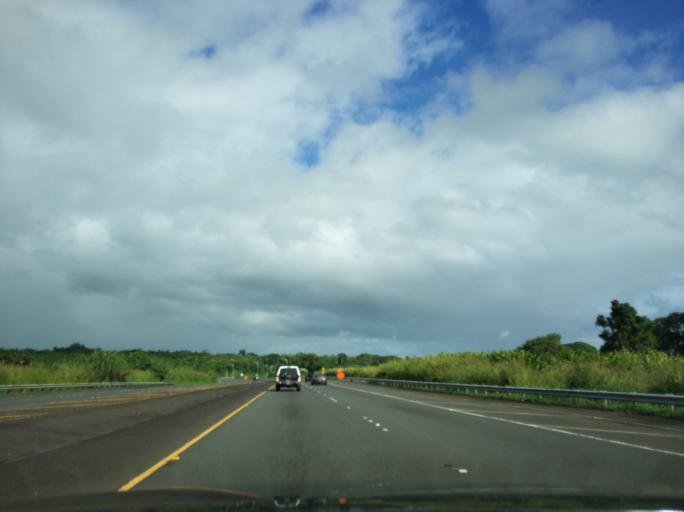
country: US
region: Hawaii
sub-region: Hawaii County
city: Kea'au
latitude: 19.6288
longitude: -155.0341
